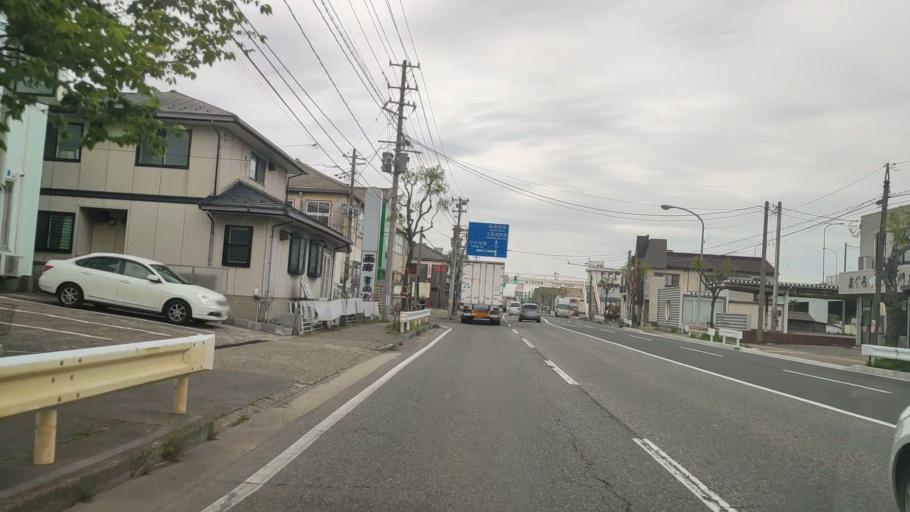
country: JP
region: Niigata
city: Niigata-shi
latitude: 37.9276
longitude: 139.0667
